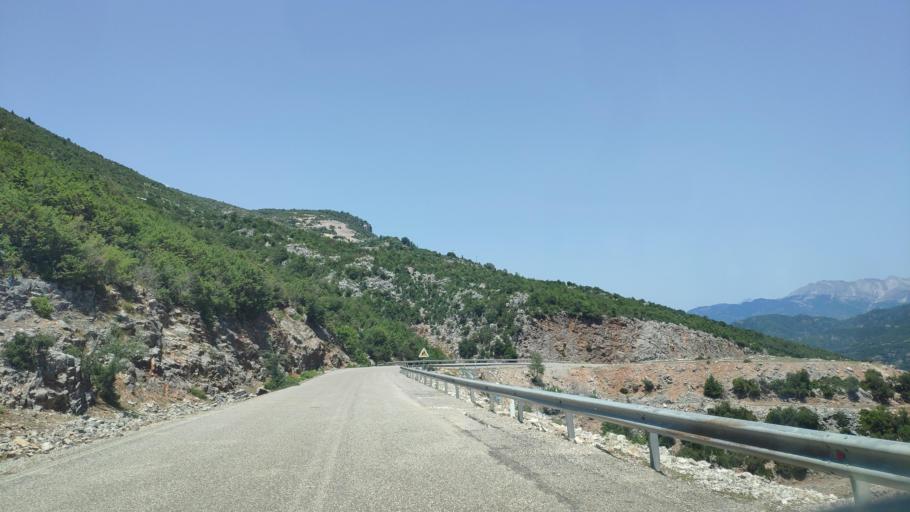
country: GR
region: Thessaly
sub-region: Nomos Kardhitsas
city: Anthiro
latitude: 39.1403
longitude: 21.3878
